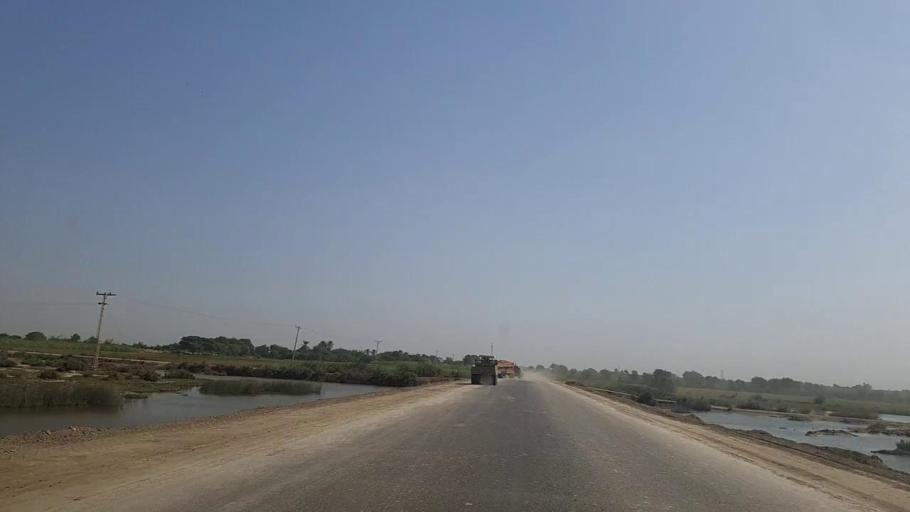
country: PK
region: Sindh
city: Mirpur Batoro
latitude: 24.7466
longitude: 68.2412
